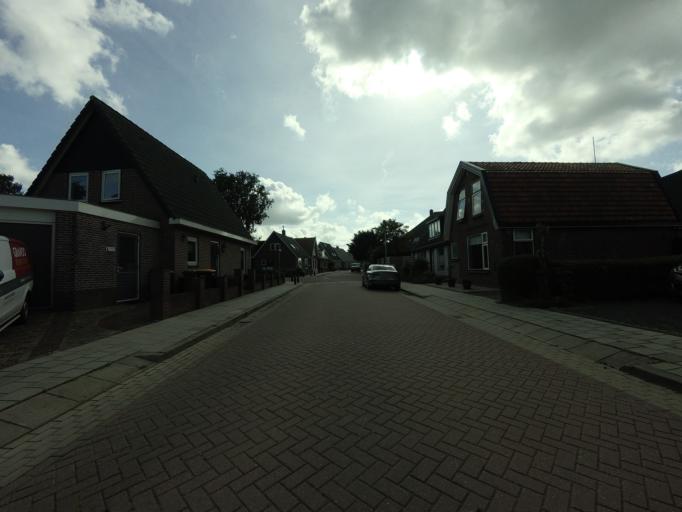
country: NL
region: North Holland
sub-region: Gemeente Hollands Kroon
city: Den Oever
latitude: 52.9100
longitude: 4.9633
